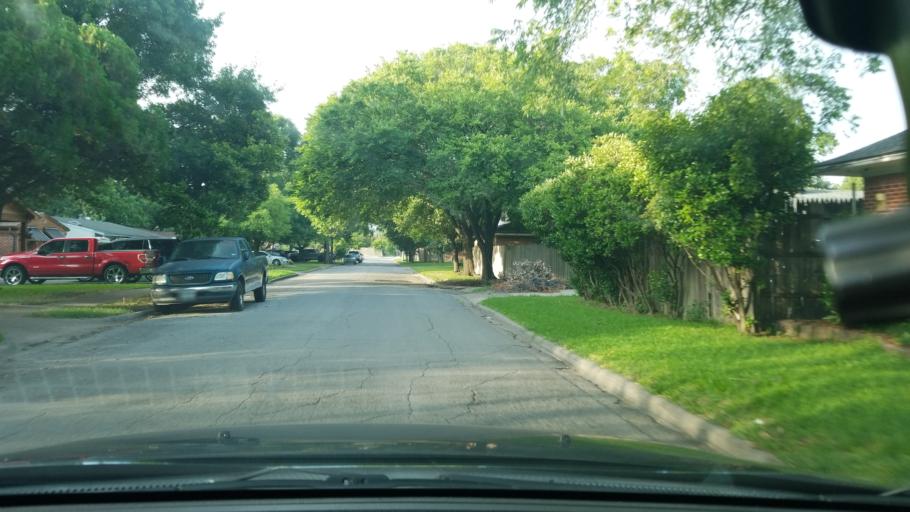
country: US
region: Texas
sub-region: Dallas County
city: Garland
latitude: 32.8294
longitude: -96.6582
